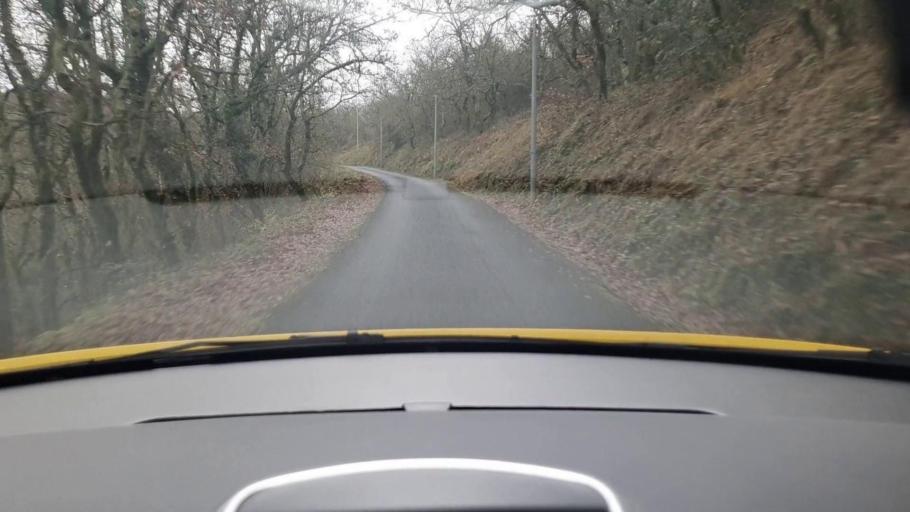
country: FR
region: Languedoc-Roussillon
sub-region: Departement du Gard
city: Molieres-sur-Ceze
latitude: 44.2698
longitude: 4.1285
